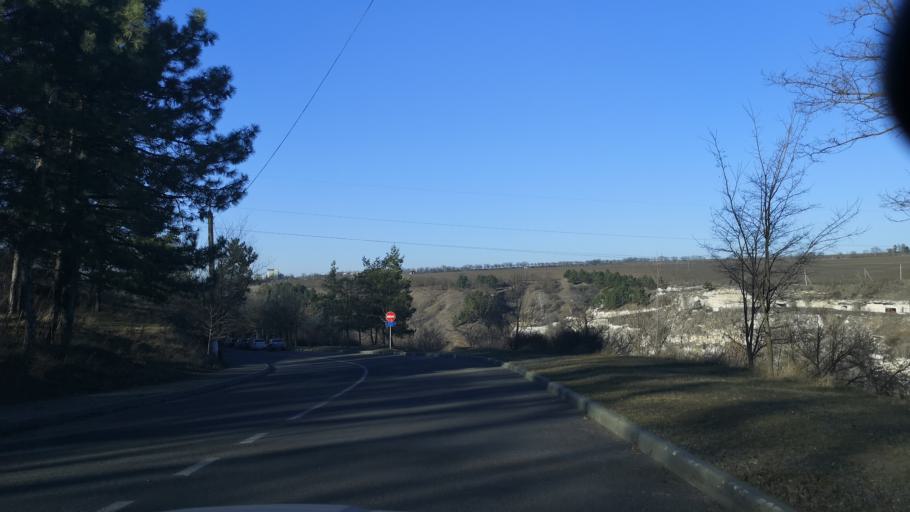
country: MD
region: Chisinau
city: Cricova
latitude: 47.1464
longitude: 28.8631
